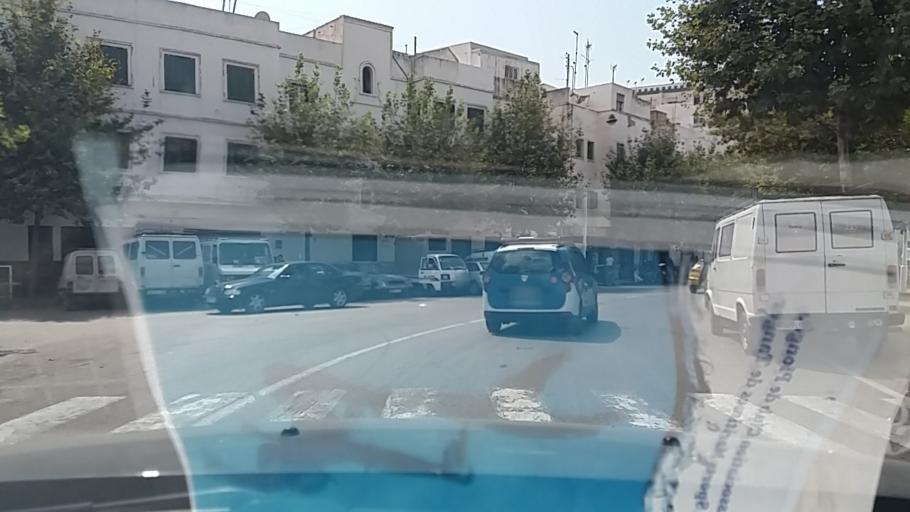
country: MA
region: Tanger-Tetouan
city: Tetouan
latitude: 35.5700
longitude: -5.3621
